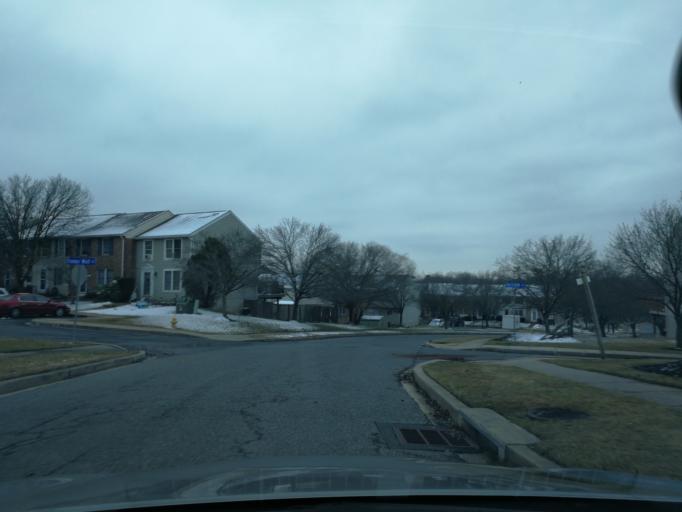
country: US
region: Maryland
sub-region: Harford County
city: Bel Air South
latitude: 39.4722
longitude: -76.2953
